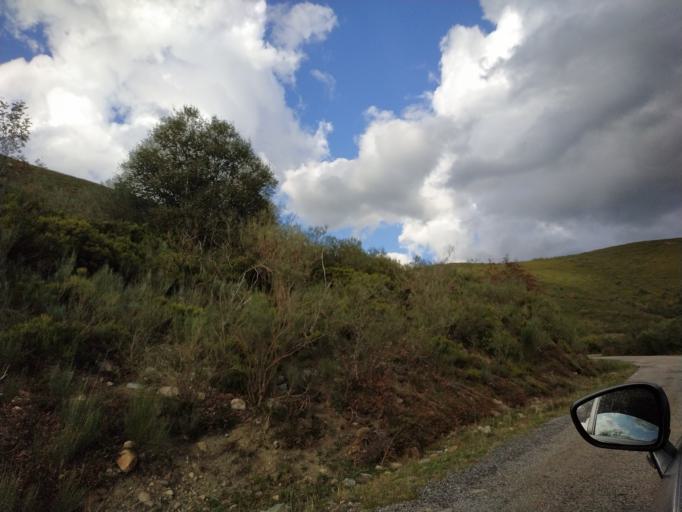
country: ES
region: Castille and Leon
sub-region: Provincia de Leon
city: Candin
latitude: 42.8682
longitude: -6.8394
